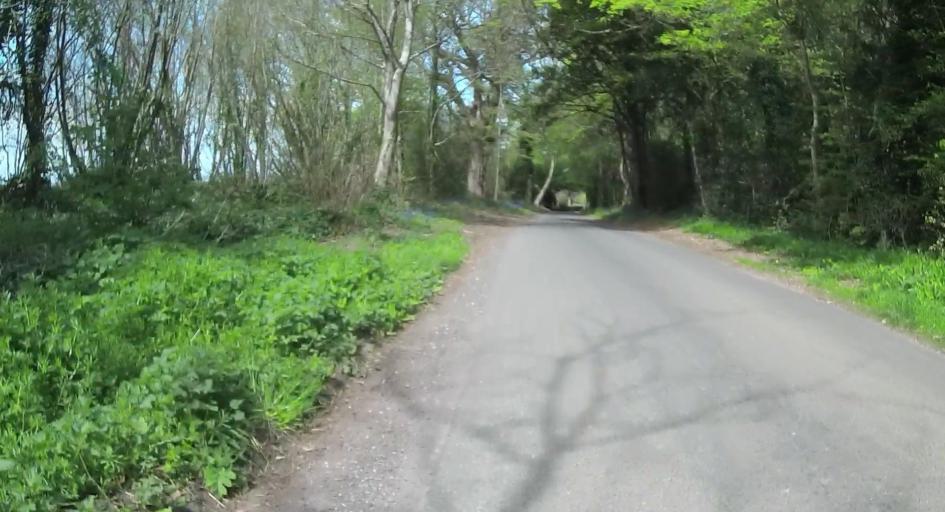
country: GB
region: England
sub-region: Hampshire
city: Chandlers Ford
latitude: 51.0740
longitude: -1.4516
